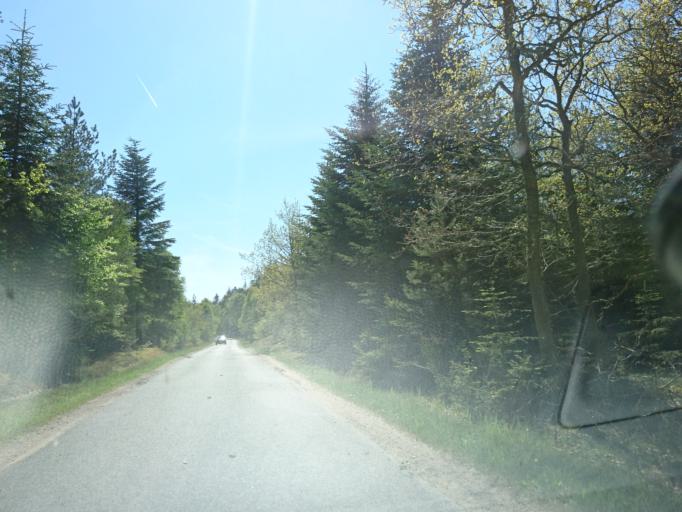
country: DK
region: North Denmark
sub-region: Hjorring Kommune
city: Sindal
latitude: 57.5964
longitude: 10.2290
